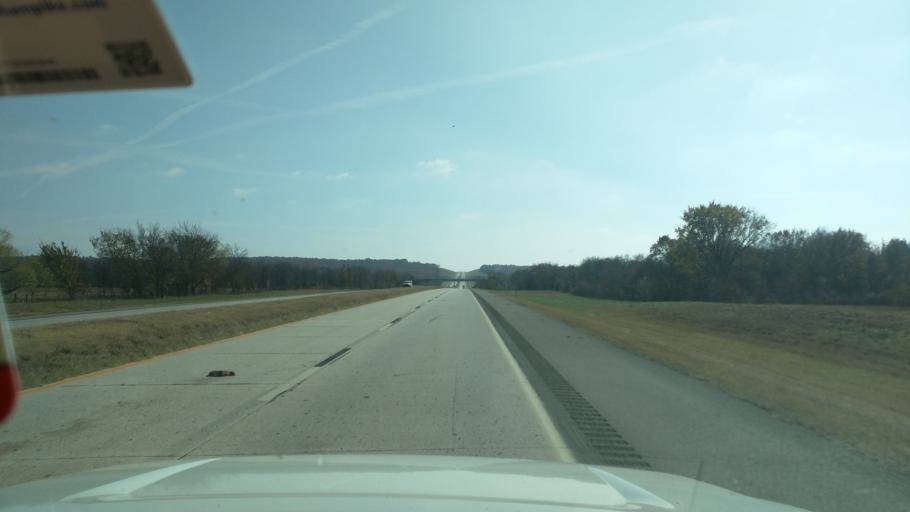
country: US
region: Oklahoma
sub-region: Muskogee County
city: Warner
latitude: 35.5575
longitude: -95.2387
